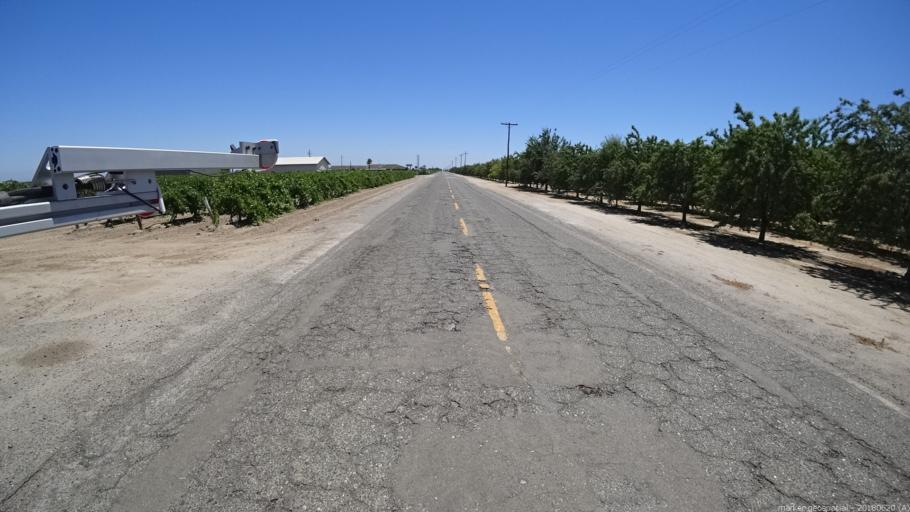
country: US
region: California
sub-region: Madera County
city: Parkwood
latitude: 36.8659
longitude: -120.0531
